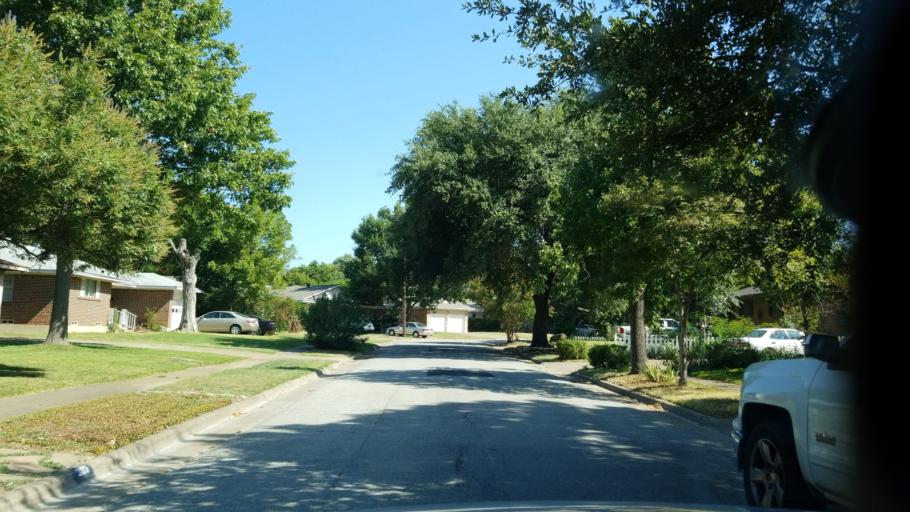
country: US
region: Texas
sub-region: Dallas County
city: Duncanville
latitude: 32.6442
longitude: -96.9042
